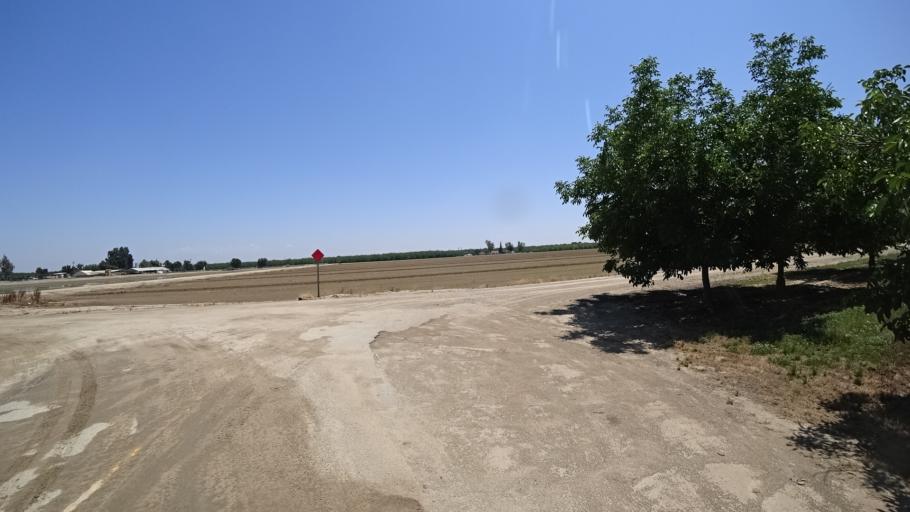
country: US
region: California
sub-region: Fresno County
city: Laton
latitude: 36.4122
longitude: -119.7182
